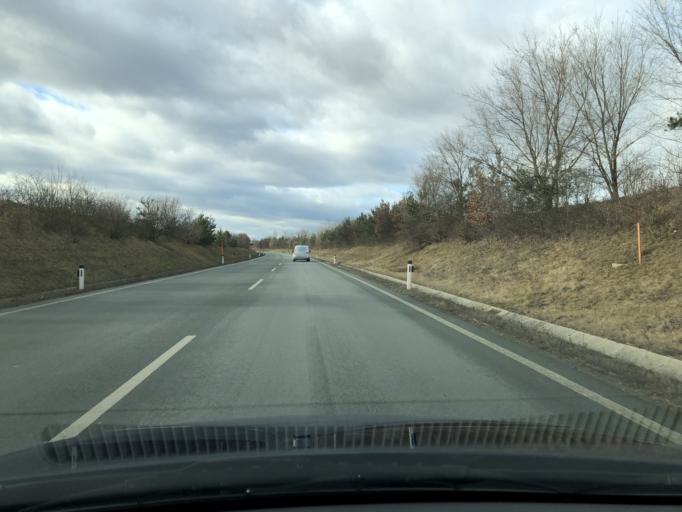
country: AT
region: Burgenland
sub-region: Politischer Bezirk Oberwart
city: Markt Neuhodis
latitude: 47.2721
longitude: 16.3859
